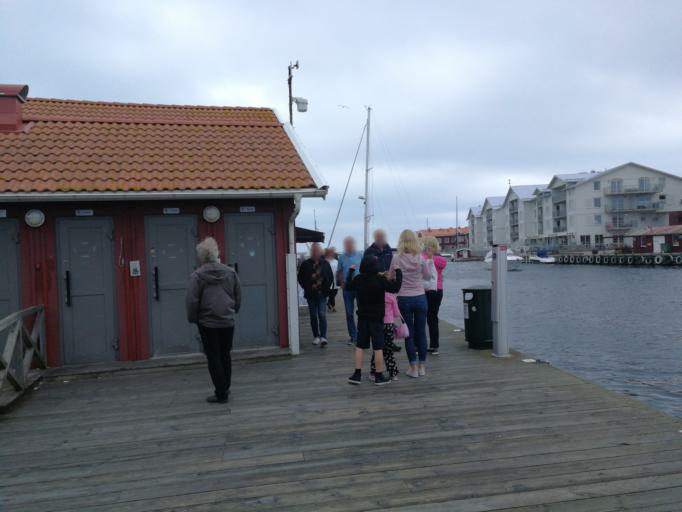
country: SE
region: Vaestra Goetaland
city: Smoegen
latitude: 58.3534
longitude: 11.2230
